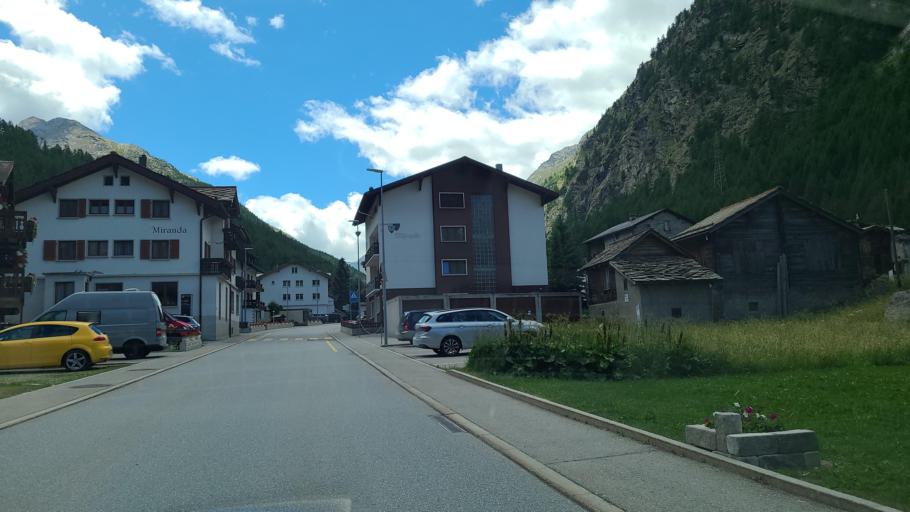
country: CH
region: Valais
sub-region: Visp District
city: Saas-Fee
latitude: 46.0969
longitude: 7.9573
